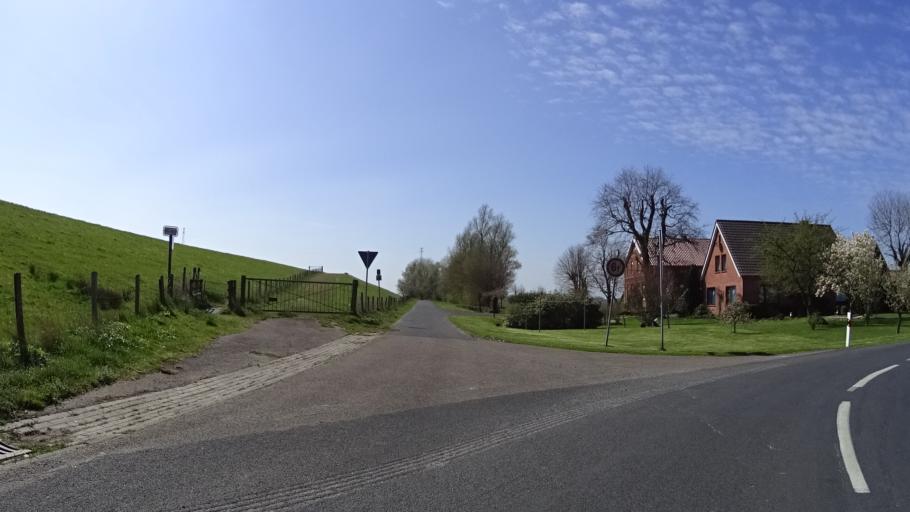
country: DE
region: Lower Saxony
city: Weener
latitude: 53.1849
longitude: 7.3911
